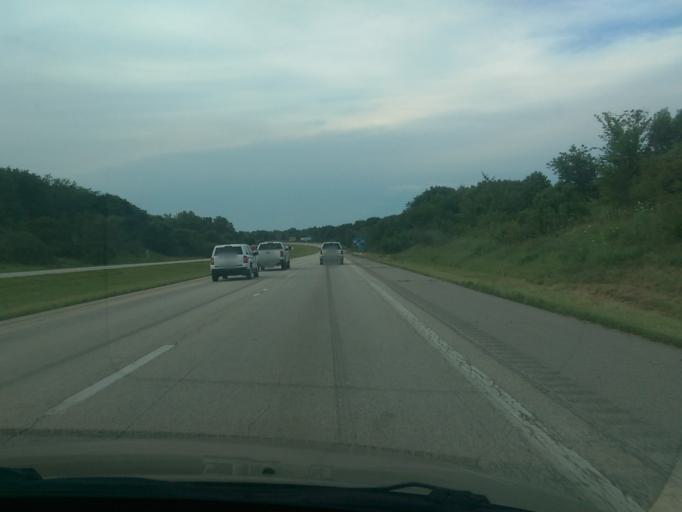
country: US
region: Missouri
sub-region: Andrew County
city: Country Club Village
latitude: 39.8477
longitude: -94.8051
